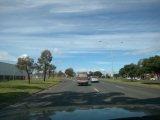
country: AU
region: Victoria
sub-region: Greater Geelong
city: Bell Park
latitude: -38.1085
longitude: 144.3534
